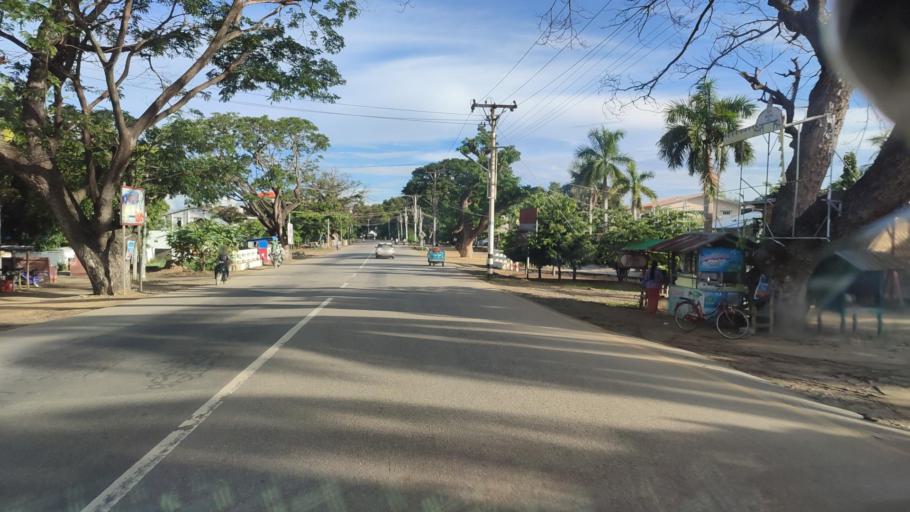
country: MM
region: Mandalay
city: Yamethin
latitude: 20.1381
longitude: 96.1971
